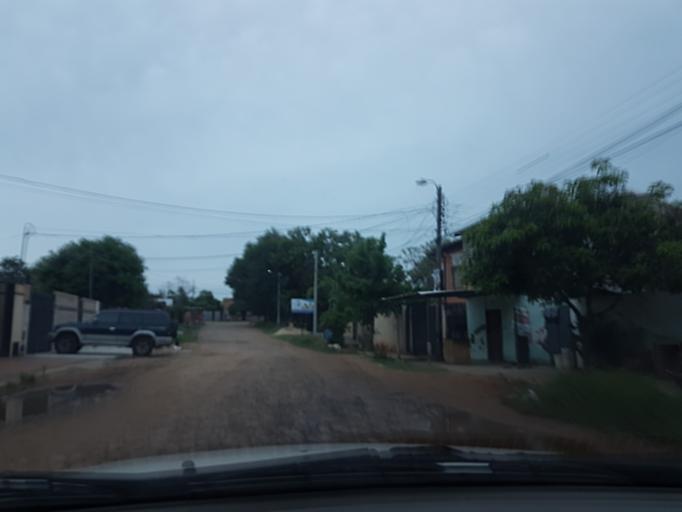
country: PY
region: Central
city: Colonia Mariano Roque Alonso
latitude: -25.2369
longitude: -57.5367
